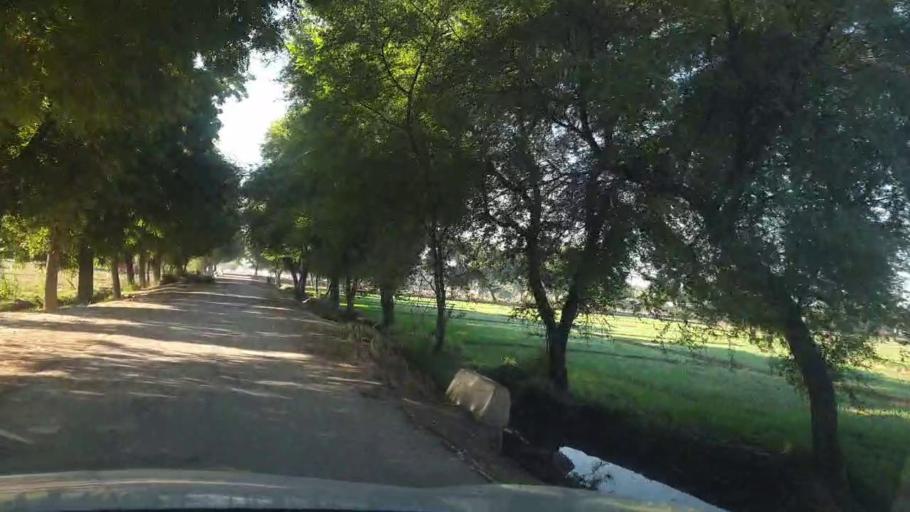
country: PK
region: Sindh
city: Bhan
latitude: 26.5471
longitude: 67.6751
